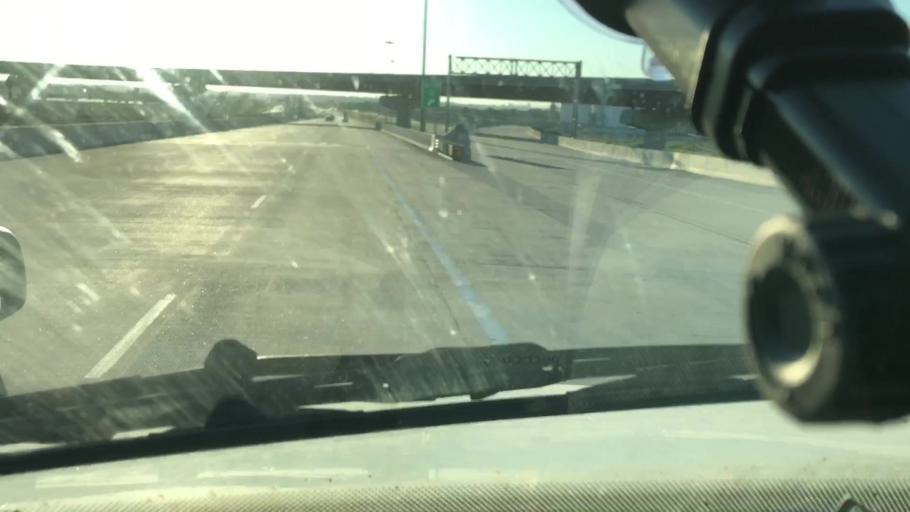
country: US
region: Iowa
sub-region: Pottawattamie County
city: Council Bluffs
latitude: 41.2321
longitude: -95.8373
